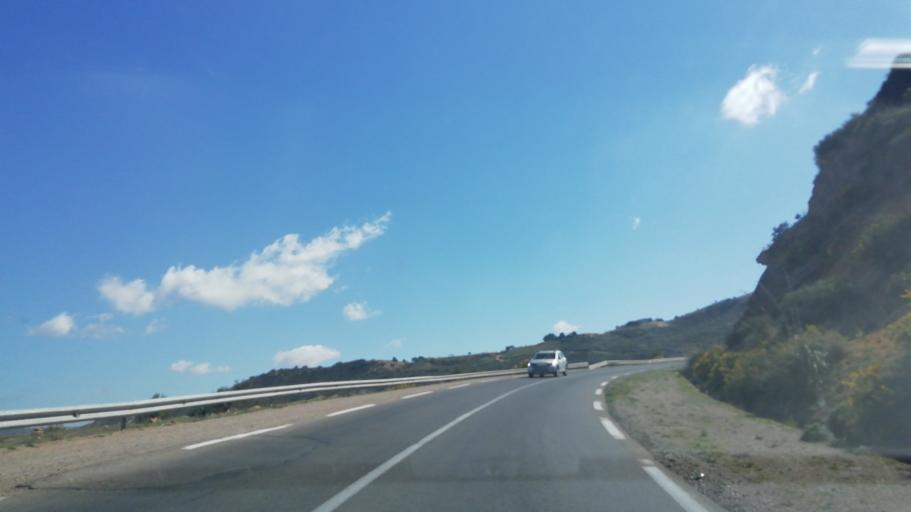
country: DZ
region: Mascara
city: Mascara
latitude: 35.4816
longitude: 0.1592
